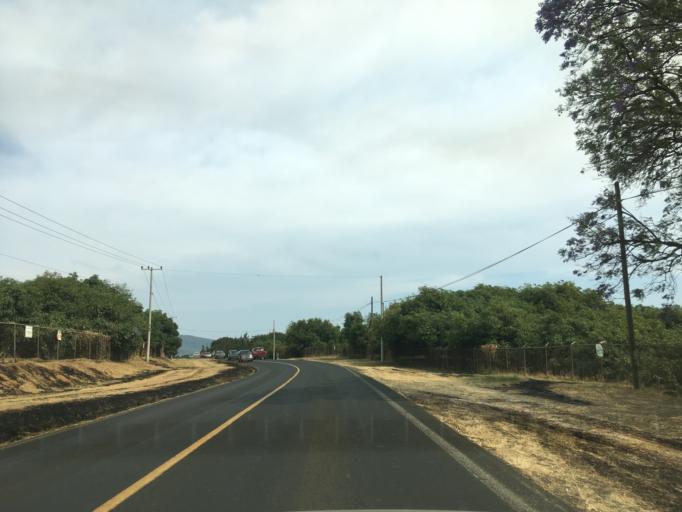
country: MX
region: Michoacan
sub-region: Uruapan
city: Uruapan
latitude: 19.3855
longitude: -102.0951
